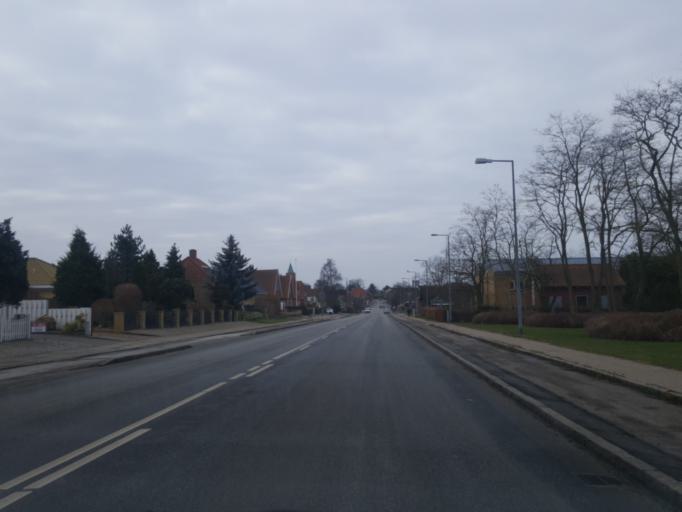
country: DK
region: Zealand
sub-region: Vordingborg Kommune
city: Vordingborg
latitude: 55.0128
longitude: 11.9186
